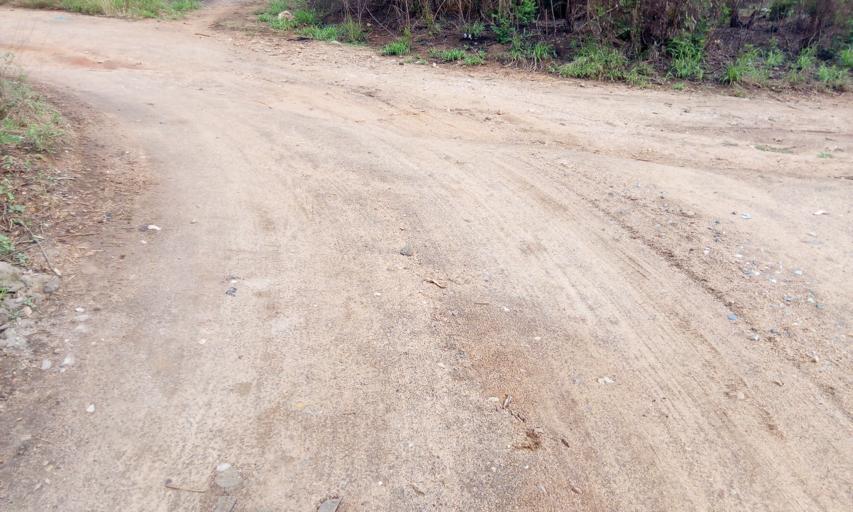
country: GH
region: Central
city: Winneba
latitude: 5.3618
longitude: -0.6202
